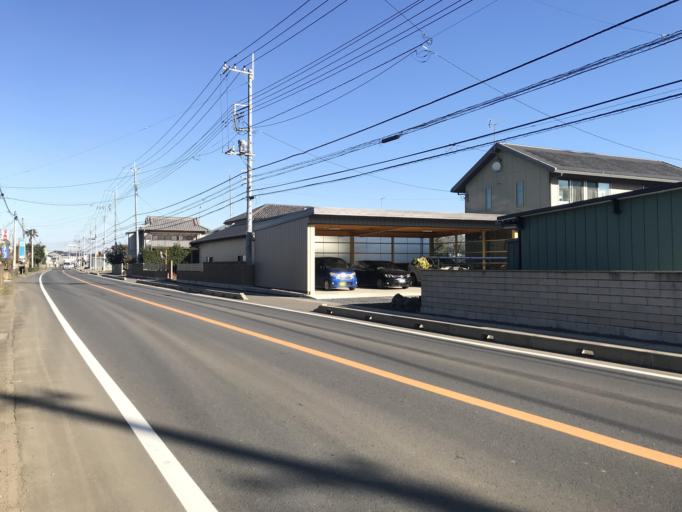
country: JP
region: Tochigi
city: Oyama
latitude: 36.2134
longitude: 139.8230
